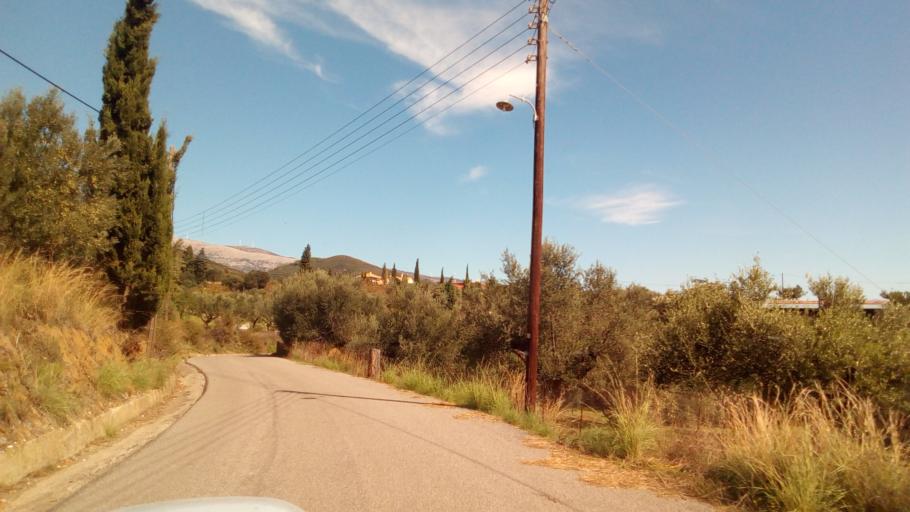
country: GR
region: West Greece
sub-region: Nomos Aitolias kai Akarnanias
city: Antirrio
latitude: 38.3620
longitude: 21.7614
